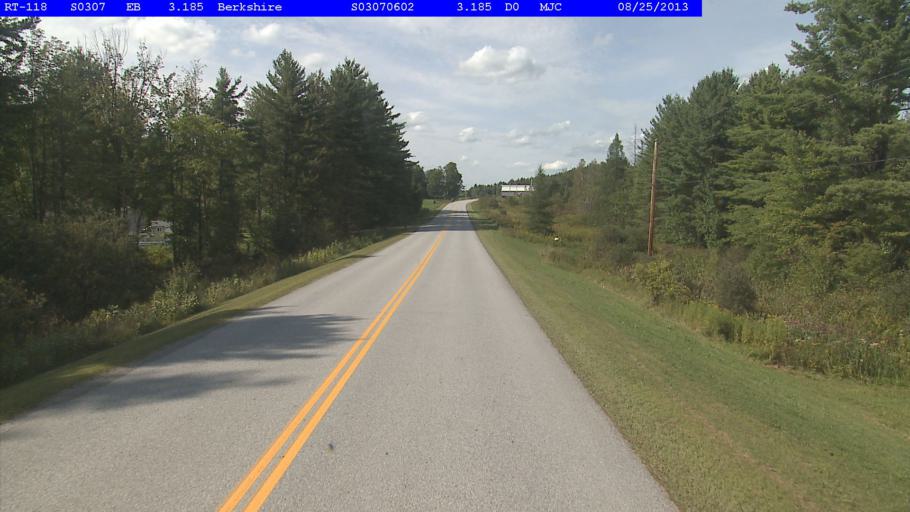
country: US
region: Vermont
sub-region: Franklin County
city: Enosburg Falls
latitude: 44.9614
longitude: -72.7578
